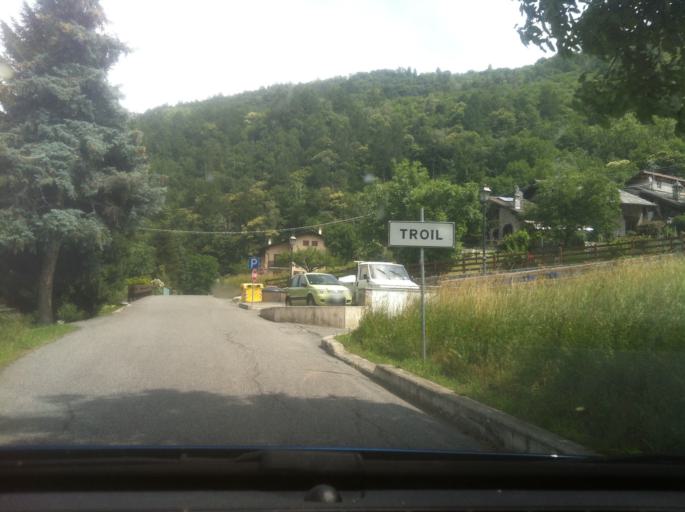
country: IT
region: Aosta Valley
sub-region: Valle d'Aosta
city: Saint Marcel
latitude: 45.7285
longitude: 7.4460
